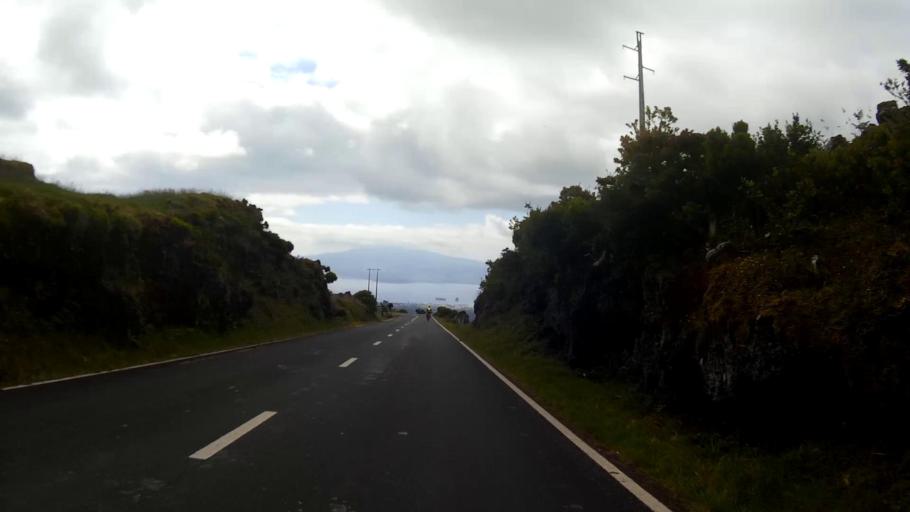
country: PT
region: Azores
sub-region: Madalena
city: Madalena
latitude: 38.4960
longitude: -28.4418
